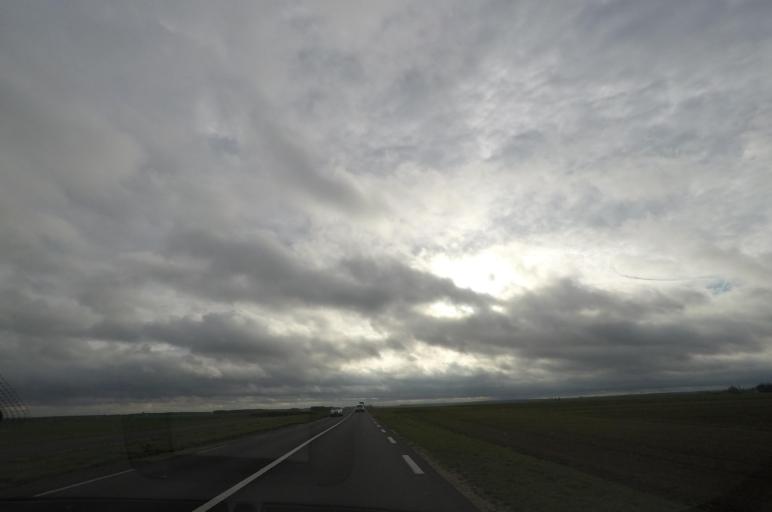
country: FR
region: Centre
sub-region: Departement du Loir-et-Cher
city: Herbault
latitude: 47.7112
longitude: 1.1645
